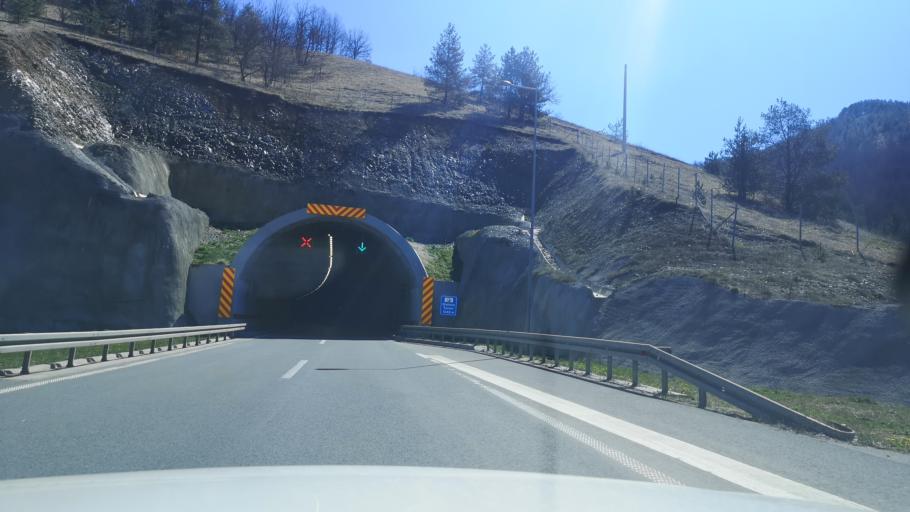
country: RS
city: Prislonica
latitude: 44.0118
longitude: 20.3658
